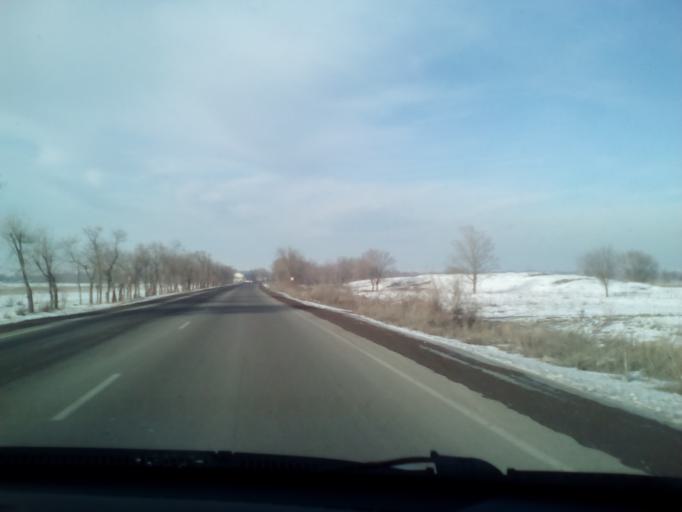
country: KZ
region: Almaty Oblysy
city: Burunday
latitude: 43.2087
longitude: 76.4150
